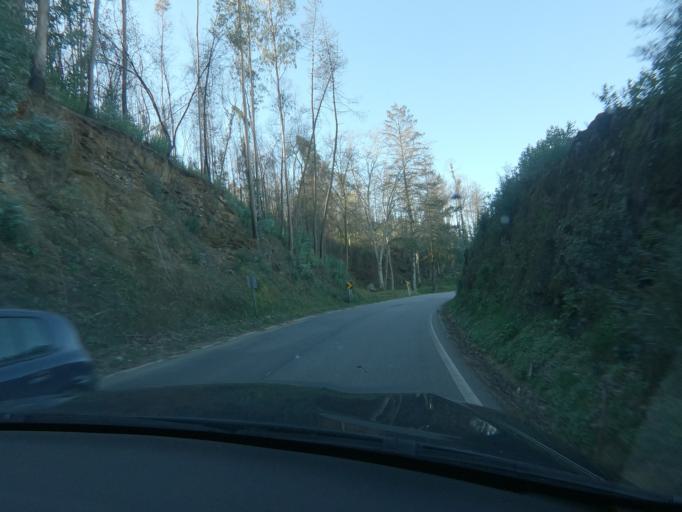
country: PT
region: Viseu
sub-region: Vouzela
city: Vouzela
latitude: 40.7271
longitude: -8.1335
